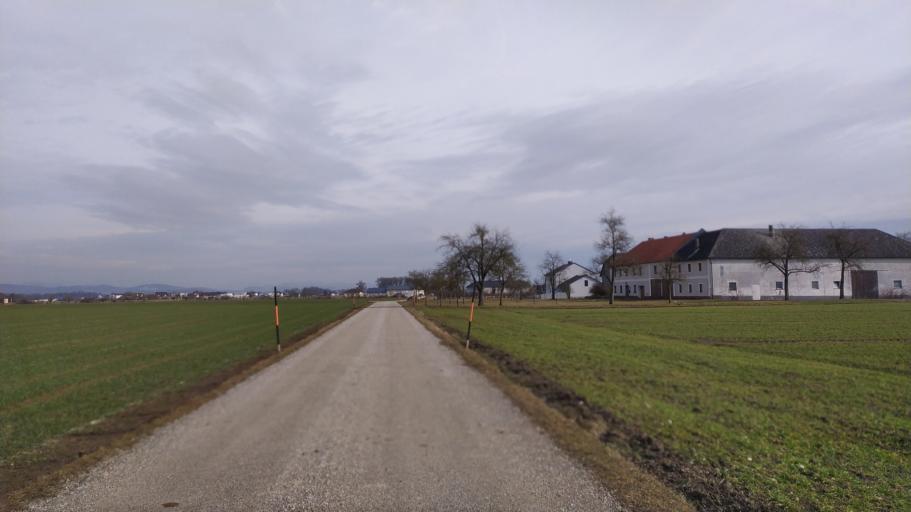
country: AT
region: Upper Austria
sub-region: Politischer Bezirk Perg
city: Perg
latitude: 48.1921
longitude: 14.6686
